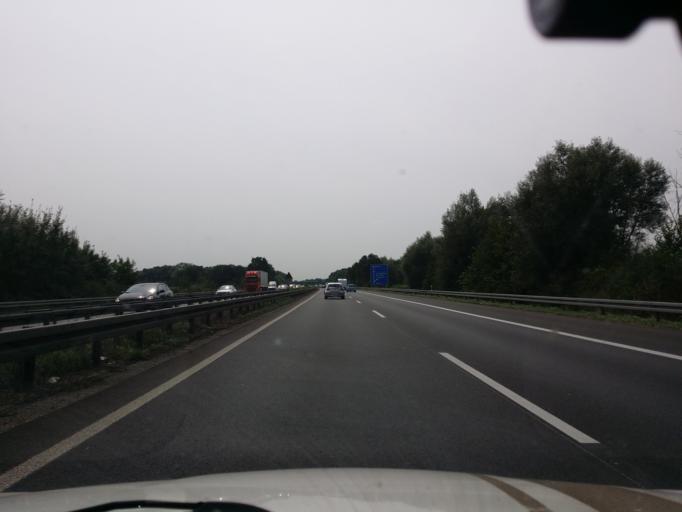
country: DE
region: Hesse
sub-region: Regierungsbezirk Darmstadt
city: Alsbach-Hahnlein
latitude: 49.7296
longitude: 8.5922
